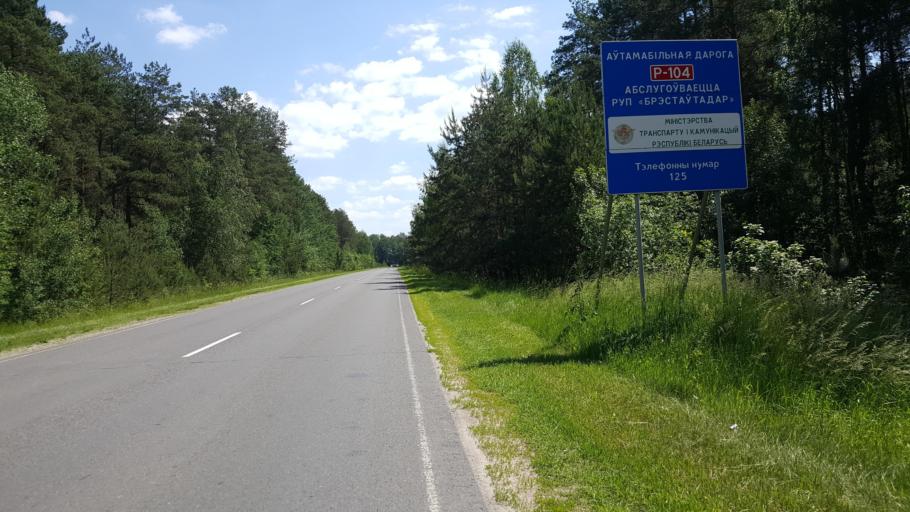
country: BY
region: Brest
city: Zhabinka
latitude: 52.2025
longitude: 24.0506
